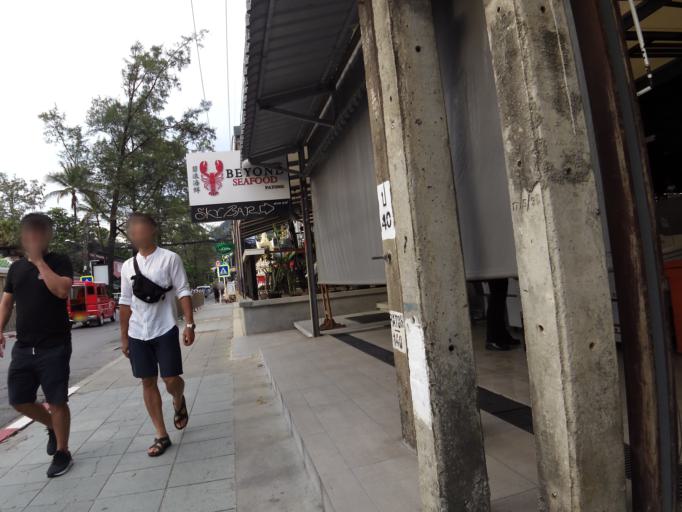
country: TH
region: Phuket
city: Patong
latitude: 7.8974
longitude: 98.2966
